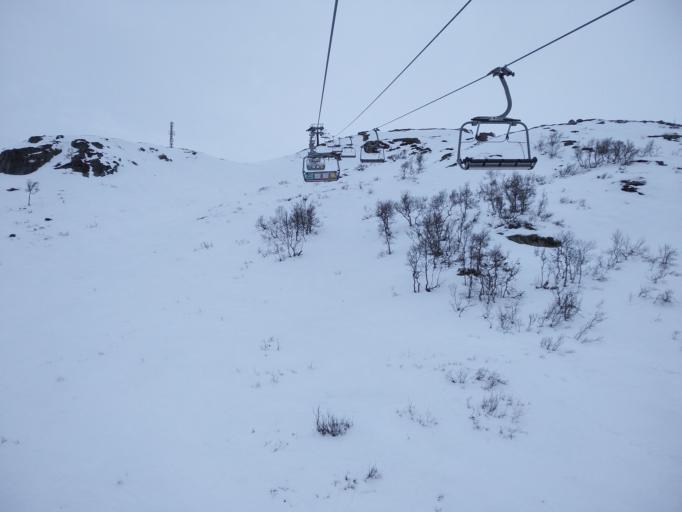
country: NO
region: Aust-Agder
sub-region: Bykle
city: Hovden
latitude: 59.5767
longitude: 7.3369
